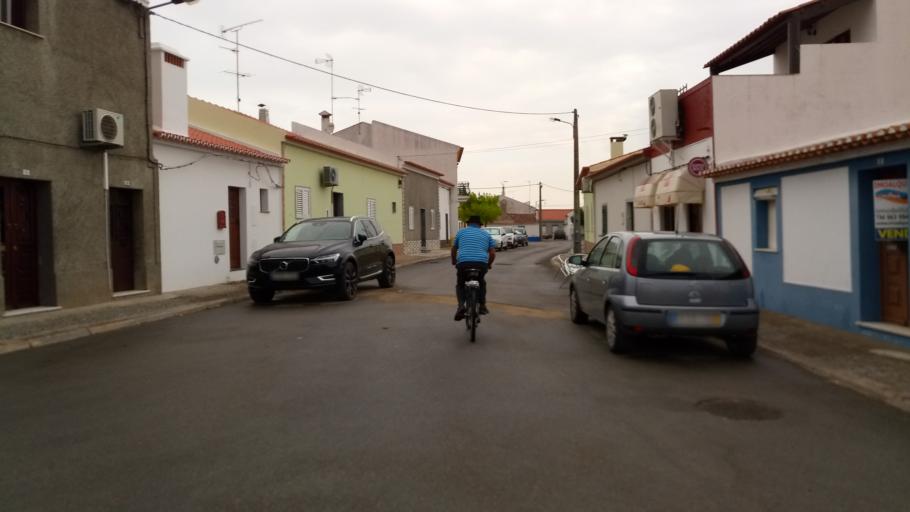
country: PT
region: Evora
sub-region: Reguengos de Monsaraz
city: Reguengos de Monsaraz
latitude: 38.3649
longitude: -7.4700
